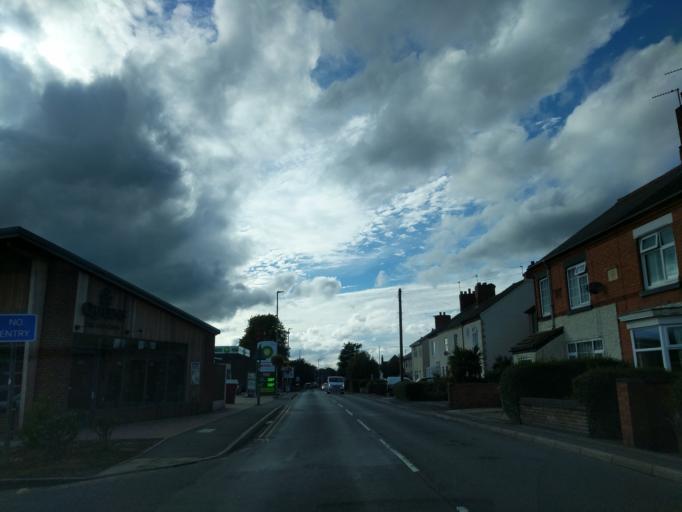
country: GB
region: England
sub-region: Leicestershire
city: Ibstock
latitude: 52.6921
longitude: -1.4001
